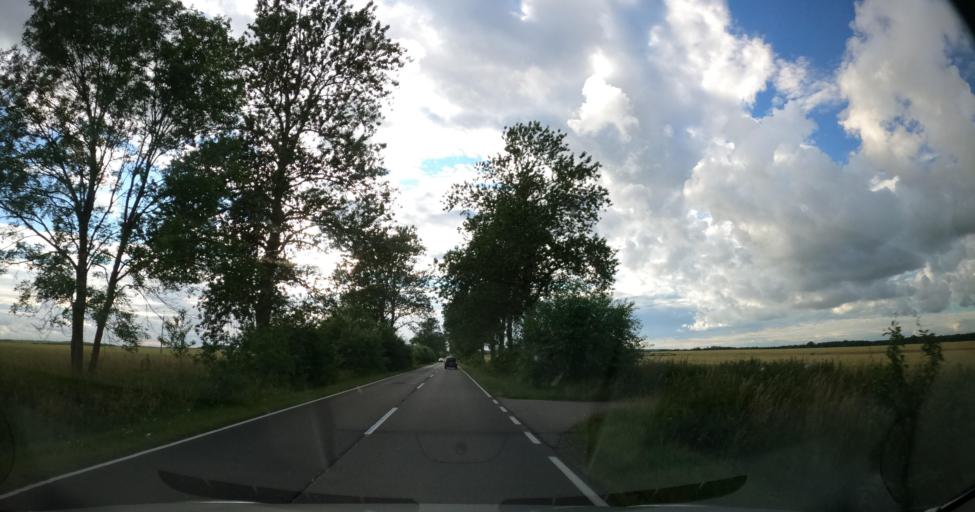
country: PL
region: Pomeranian Voivodeship
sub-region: Powiat slupski
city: Damnica
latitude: 54.4250
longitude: 17.3734
